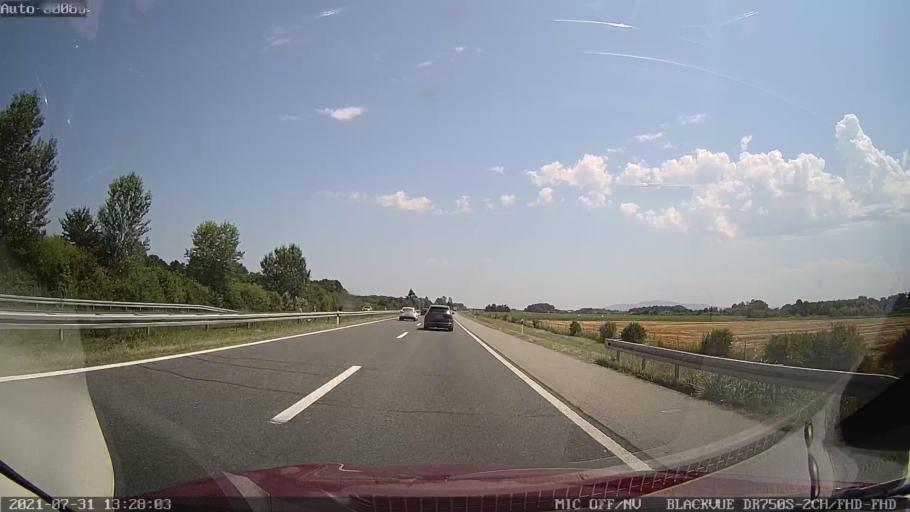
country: HR
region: Brodsko-Posavska
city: Resetari
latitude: 45.2258
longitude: 17.4796
